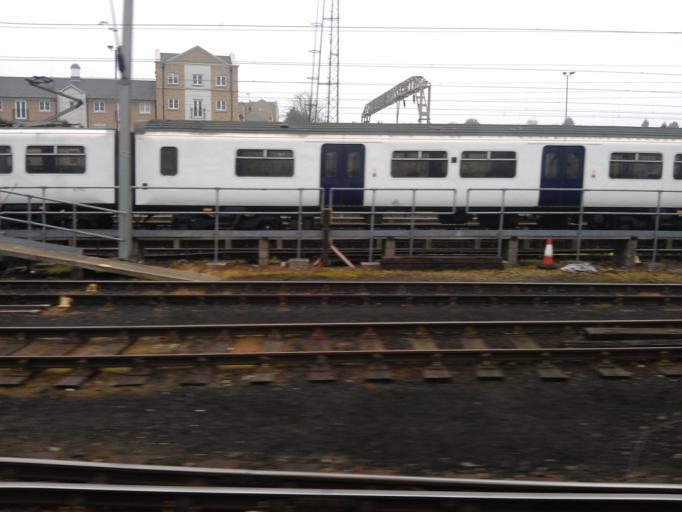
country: GB
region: England
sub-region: Essex
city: Colchester
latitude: 51.9018
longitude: 0.8855
